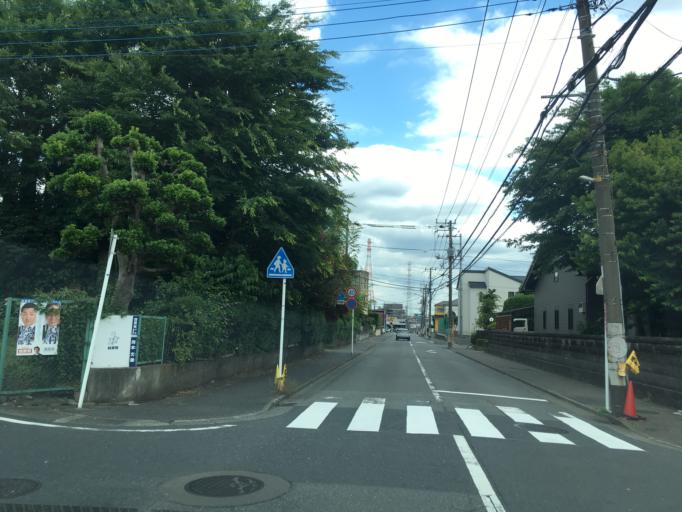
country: JP
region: Tokyo
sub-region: Machida-shi
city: Machida
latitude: 35.5630
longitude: 139.4032
